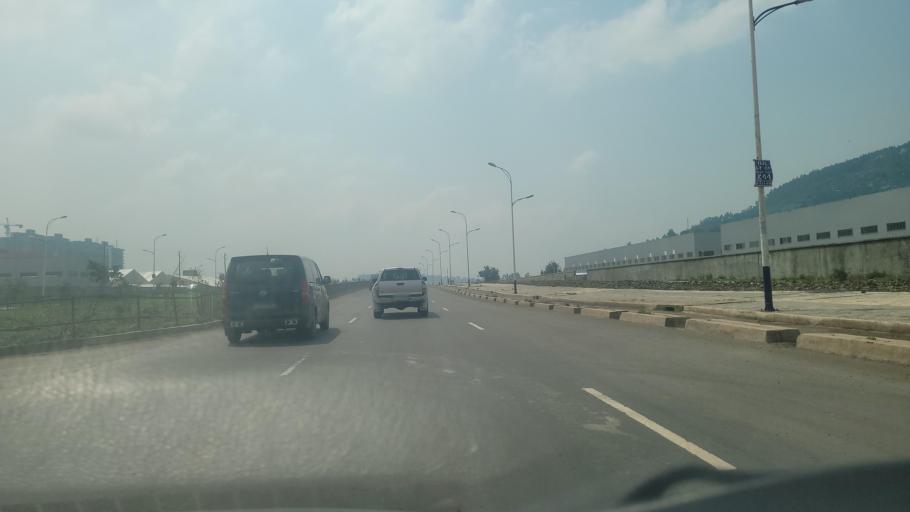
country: ET
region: Adis Abeba
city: Addis Ababa
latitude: 8.9504
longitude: 38.7030
